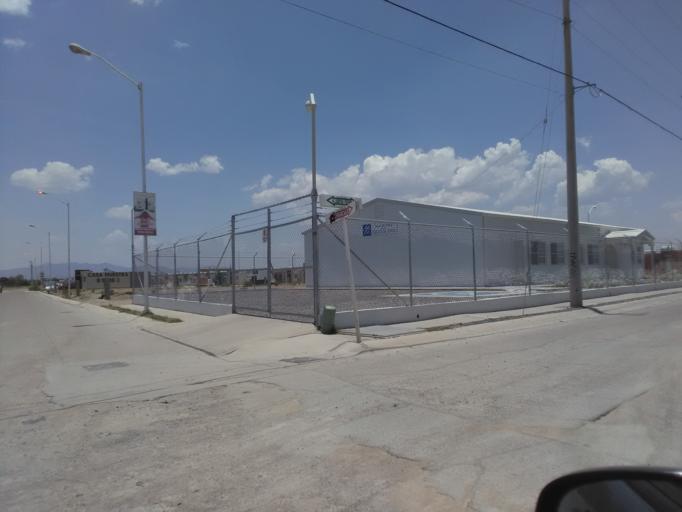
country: MX
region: Durango
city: Victoria de Durango
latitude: 24.0078
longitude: -104.5995
